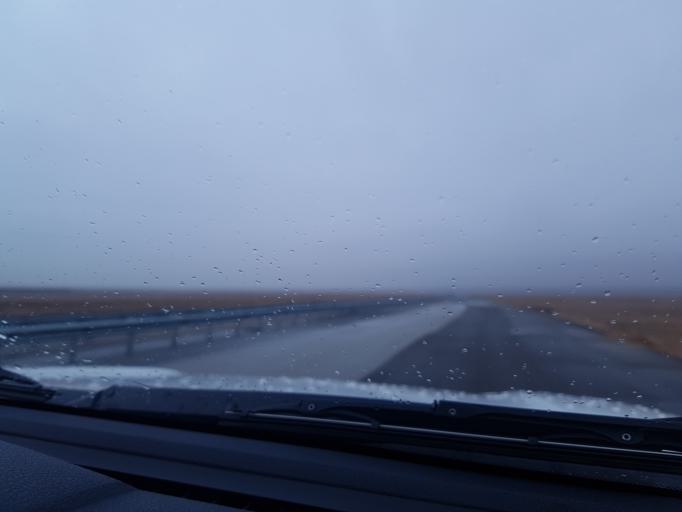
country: TM
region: Balkan
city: Balkanabat
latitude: 39.9573
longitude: 53.8289
